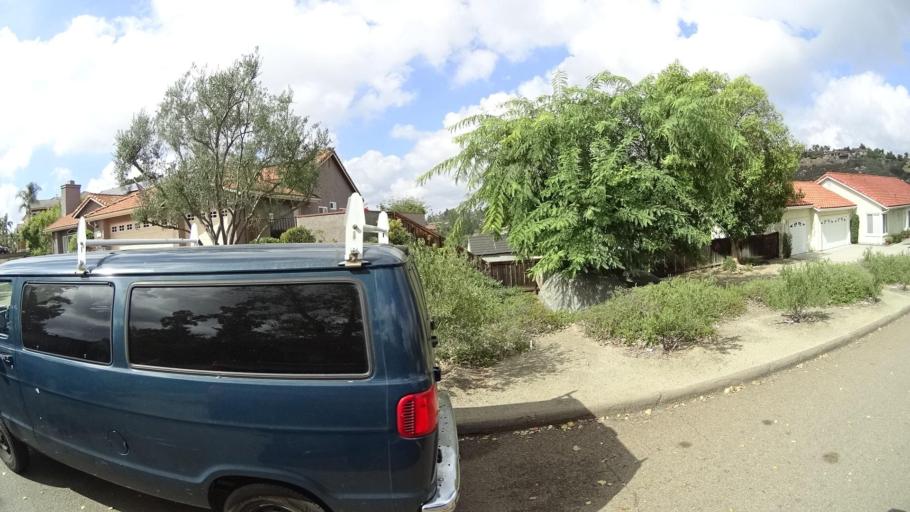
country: US
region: California
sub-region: San Diego County
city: Granite Hills
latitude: 32.7728
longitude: -116.9083
